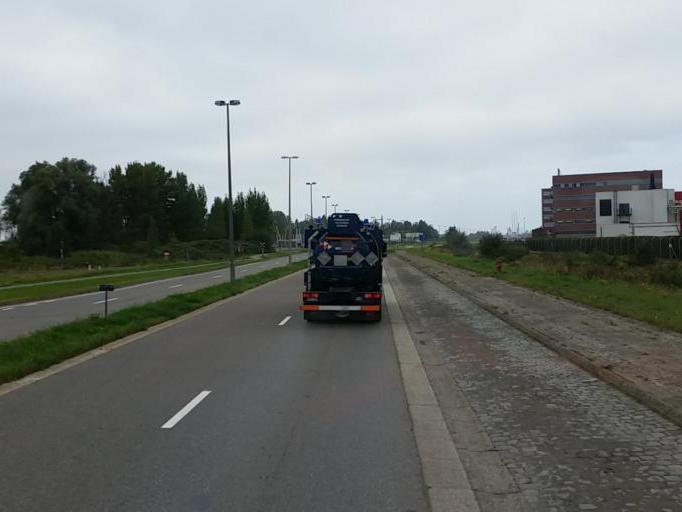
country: BE
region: Flanders
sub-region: Provincie Antwerpen
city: Zwijndrecht
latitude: 51.2812
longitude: 4.3335
